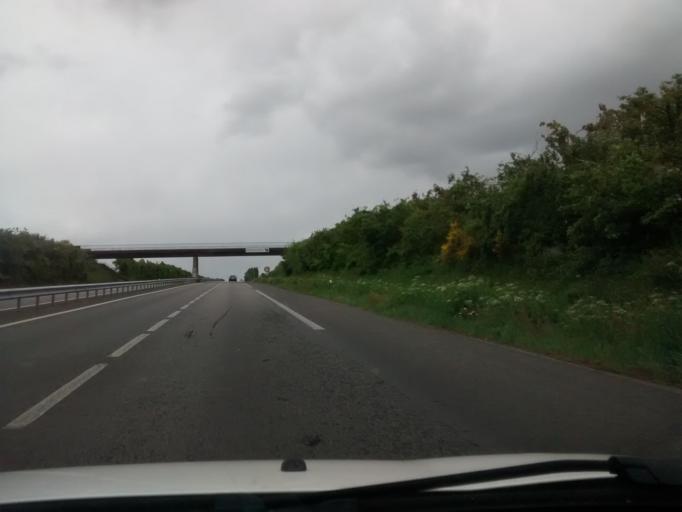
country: FR
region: Brittany
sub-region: Departement d'Ille-et-Vilaine
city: Plelan-le-Grand
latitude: 47.9683
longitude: -2.0951
